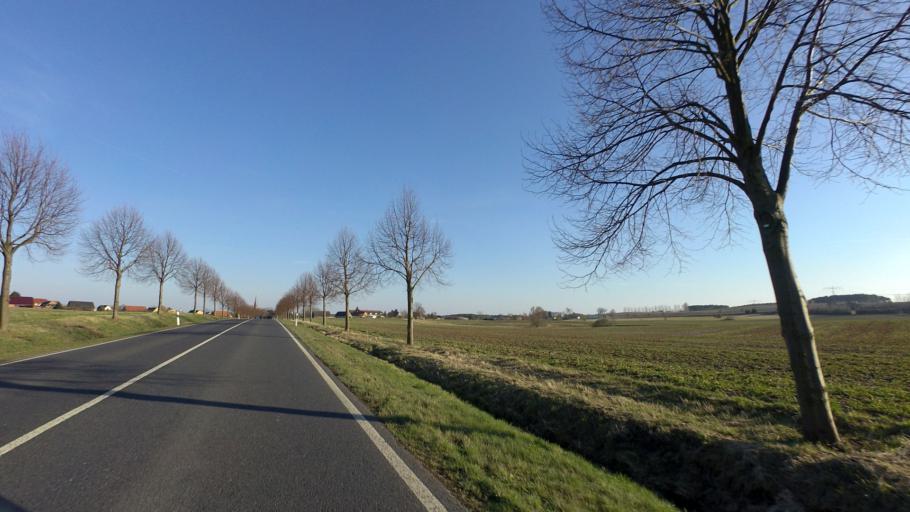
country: DE
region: Brandenburg
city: Britz
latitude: 52.9175
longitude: 13.8006
